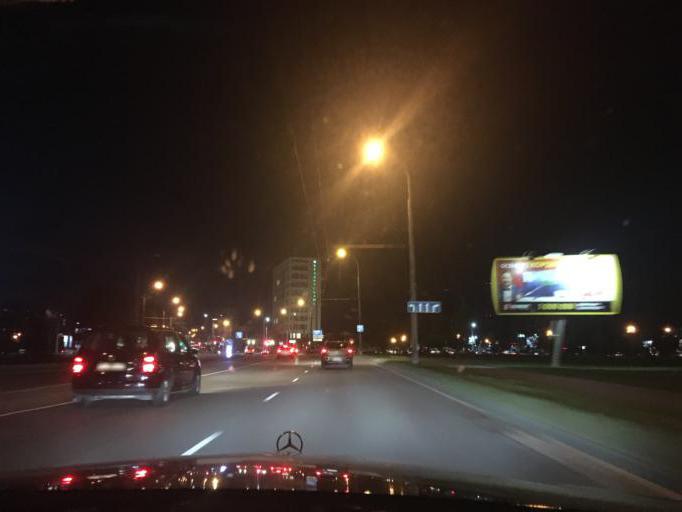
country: BY
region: Brest
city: Brest
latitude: 52.0913
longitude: 23.7332
